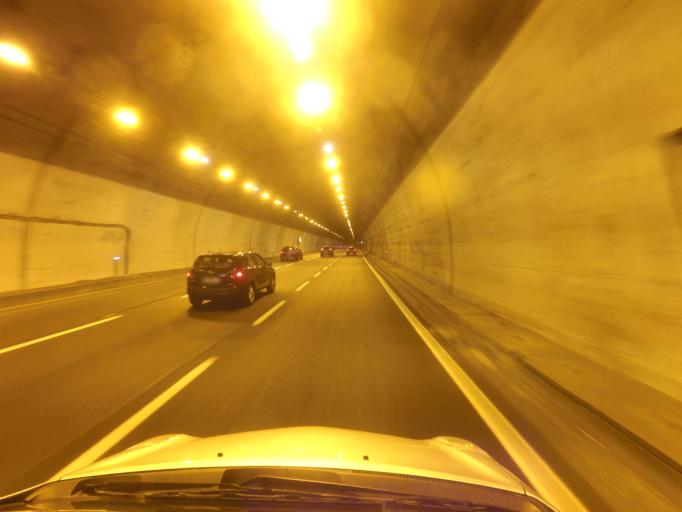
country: IT
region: Emilia-Romagna
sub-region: Provincia di Bologna
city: Vado
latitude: 44.3219
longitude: 11.2534
